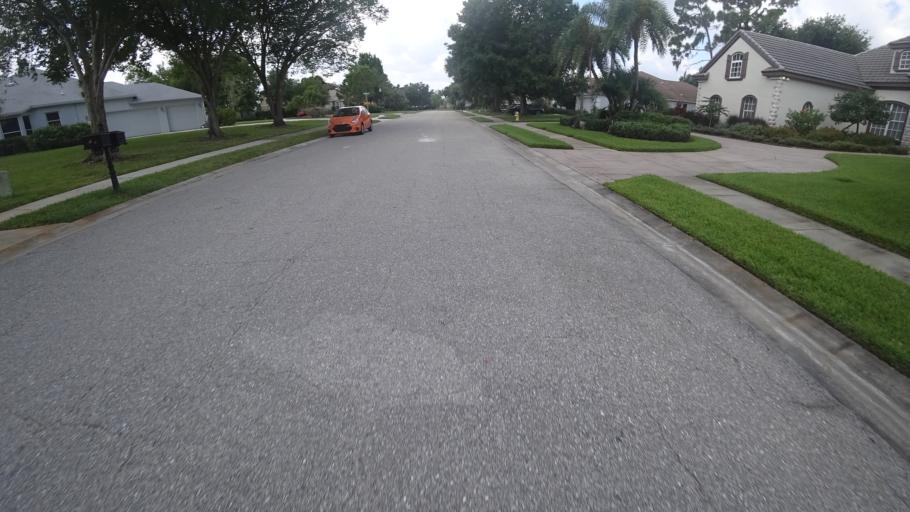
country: US
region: Florida
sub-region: Sarasota County
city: The Meadows
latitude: 27.4137
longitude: -82.4342
